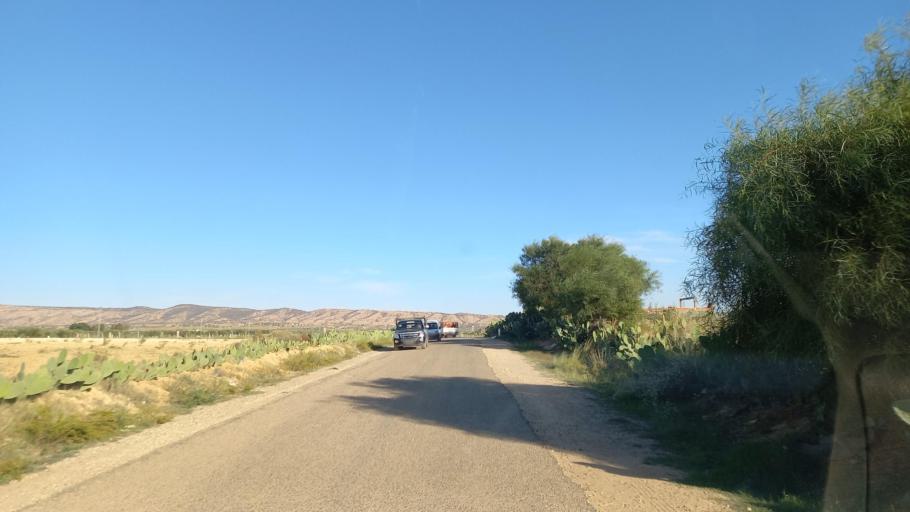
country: TN
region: Al Qasrayn
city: Sbiba
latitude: 35.3344
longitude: 9.0900
